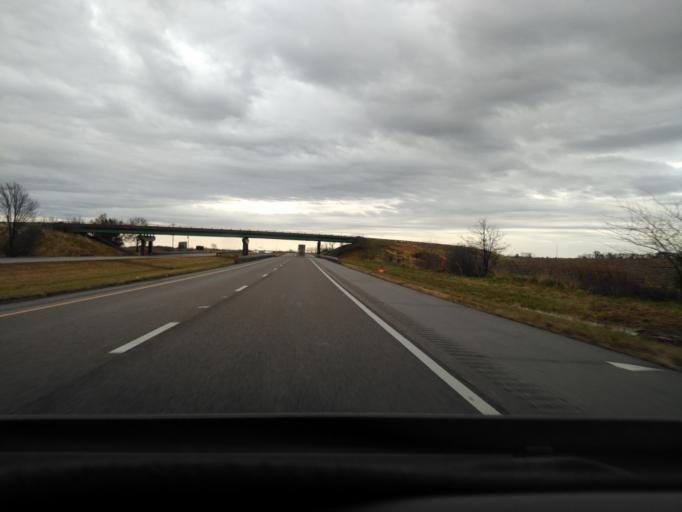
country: US
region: Illinois
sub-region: Bond County
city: Greenville
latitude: 38.8862
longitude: -89.3310
